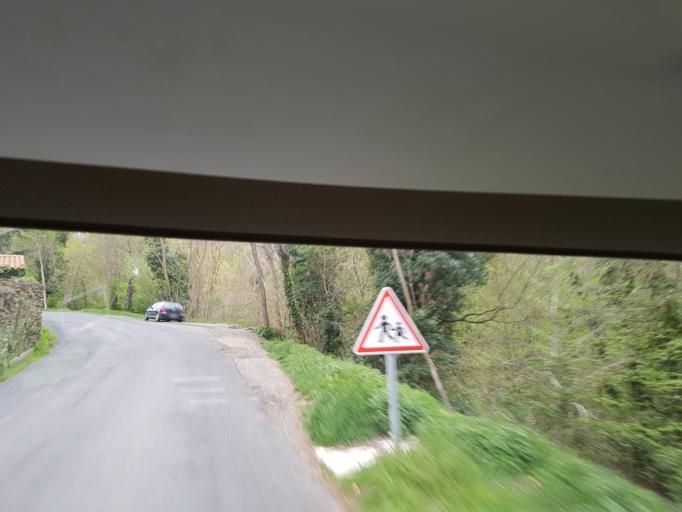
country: FR
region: Languedoc-Roussillon
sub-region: Departement des Pyrenees-Orientales
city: Ria-Sirach
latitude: 42.5965
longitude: 2.4166
